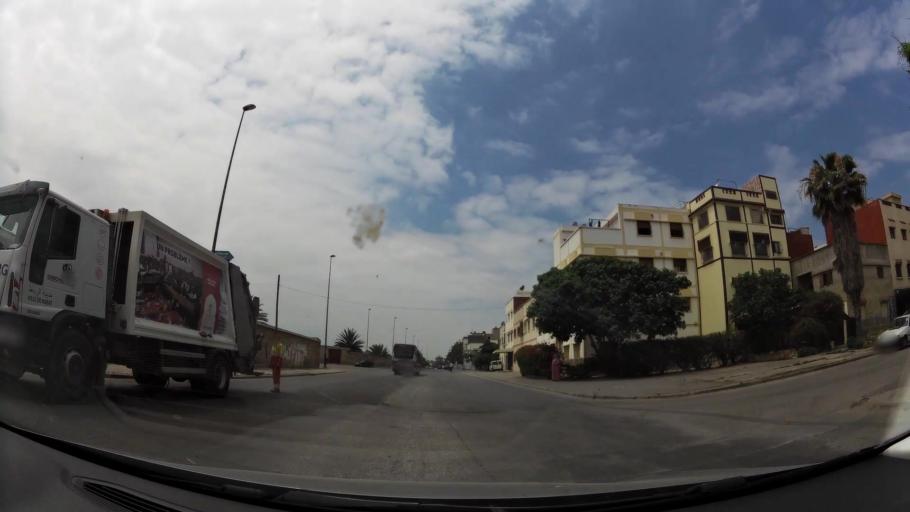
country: MA
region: Rabat-Sale-Zemmour-Zaer
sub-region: Skhirate-Temara
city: Temara
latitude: 33.9852
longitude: -6.8872
